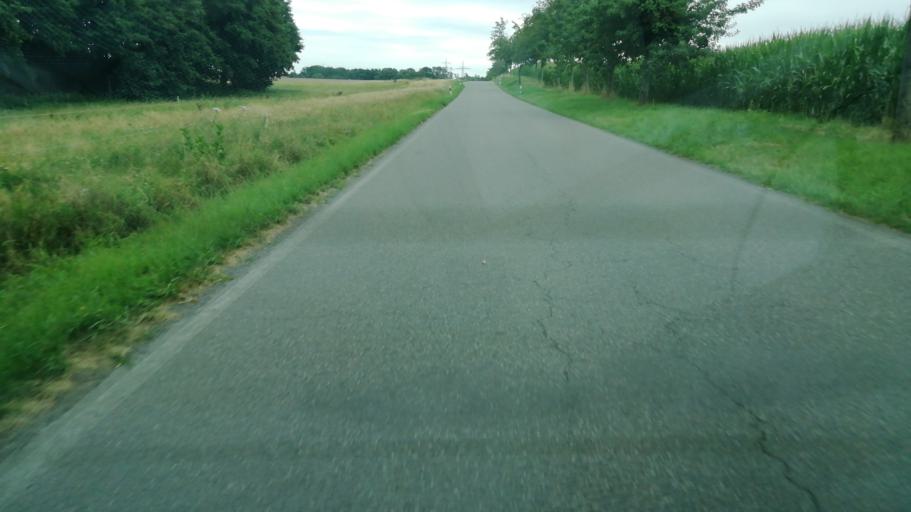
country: DE
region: Saxony
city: Wilsdruff
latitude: 51.0669
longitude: 13.5882
